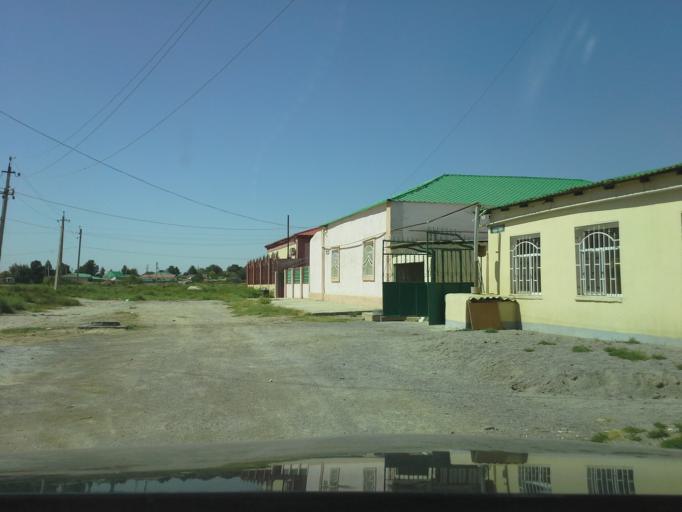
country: TM
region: Ahal
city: Ashgabat
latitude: 38.0106
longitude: 58.3058
